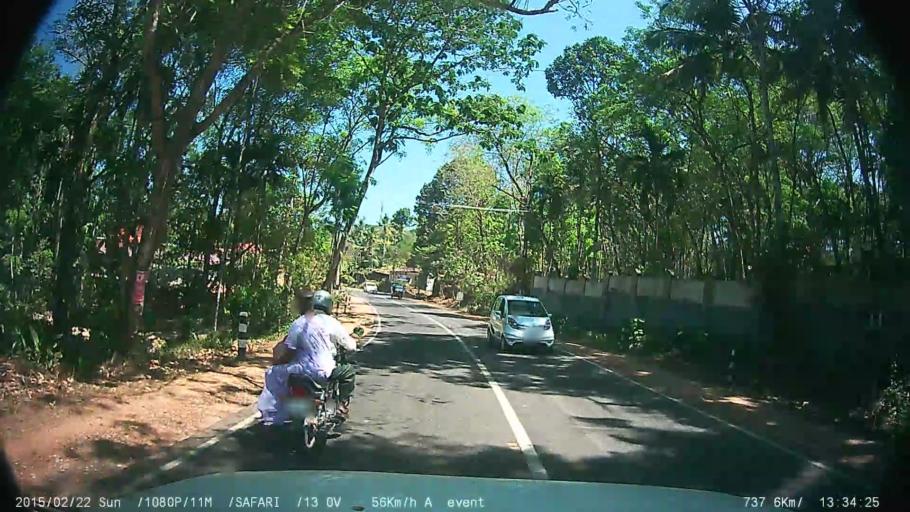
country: IN
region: Kerala
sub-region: Kottayam
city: Changanacheri
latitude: 9.4802
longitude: 76.6003
